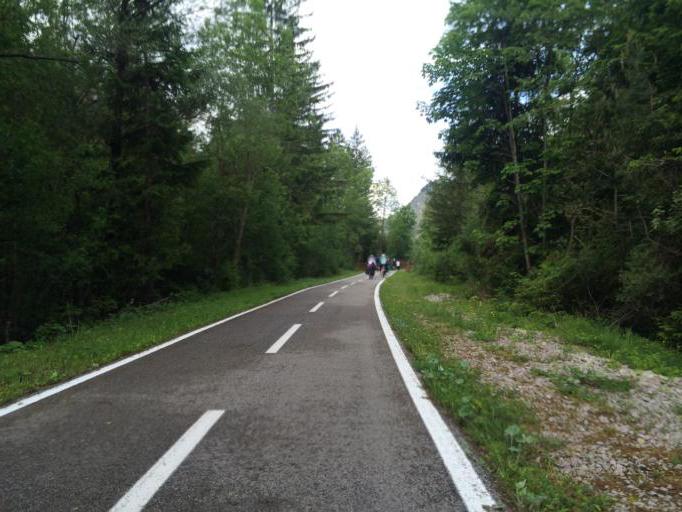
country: IT
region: Friuli Venezia Giulia
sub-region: Provincia di Udine
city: Malborghetto
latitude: 46.5030
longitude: 13.5129
